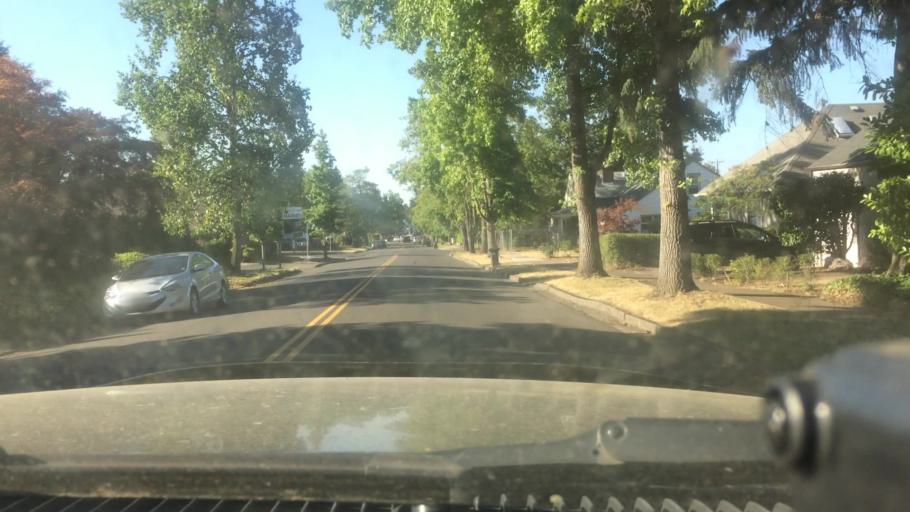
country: US
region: Oregon
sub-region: Lane County
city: Eugene
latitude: 44.0381
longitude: -123.1012
